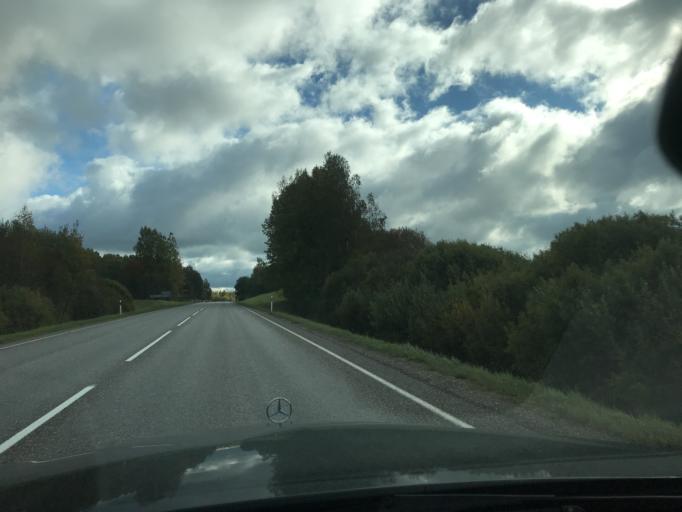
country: EE
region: Vorumaa
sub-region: Voru linn
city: Voru
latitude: 57.7581
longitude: 27.2129
